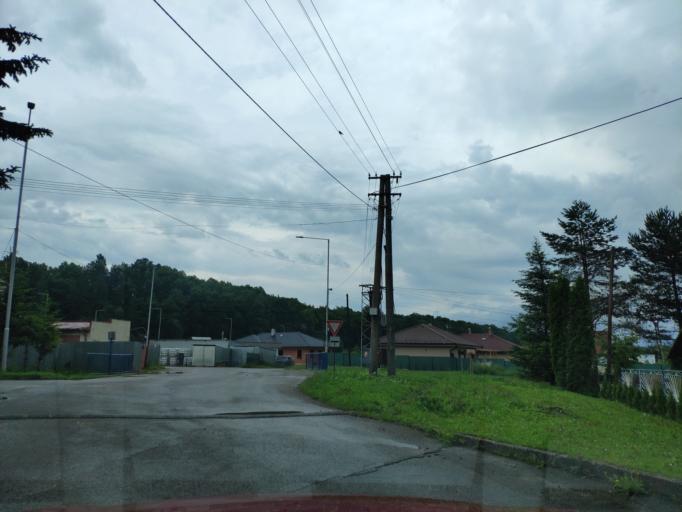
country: SK
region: Presovsky
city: Sabinov
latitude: 49.0037
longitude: 21.0908
